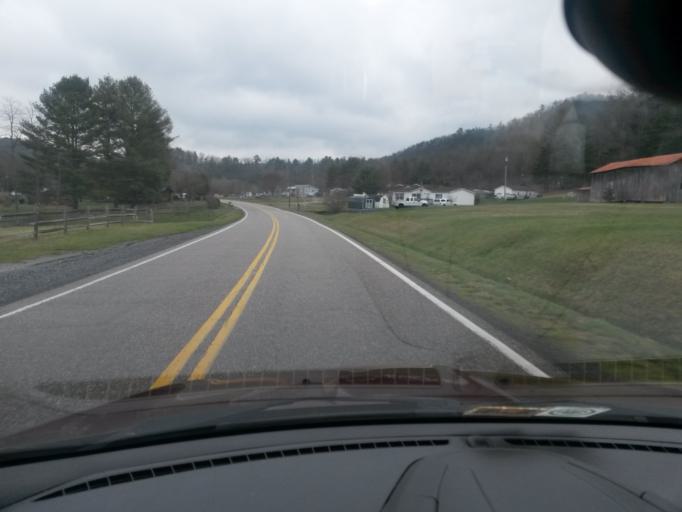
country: US
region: Virginia
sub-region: Bath County
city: Warm Springs
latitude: 37.9923
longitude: -79.6330
